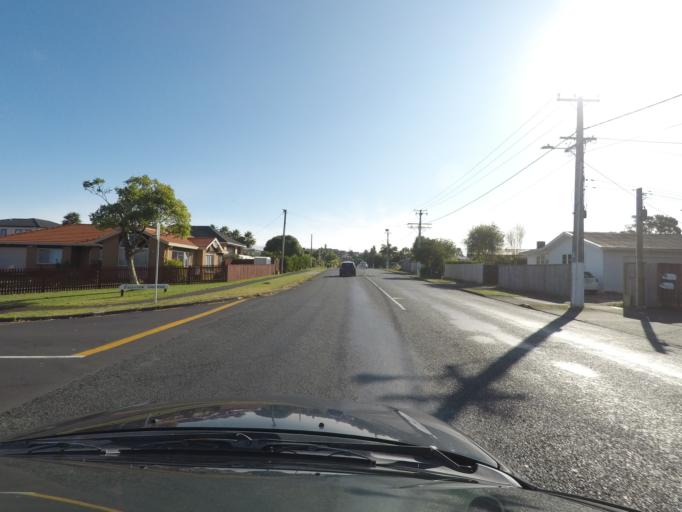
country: NZ
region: Auckland
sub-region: Auckland
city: Rosebank
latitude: -36.8665
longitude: 174.6078
